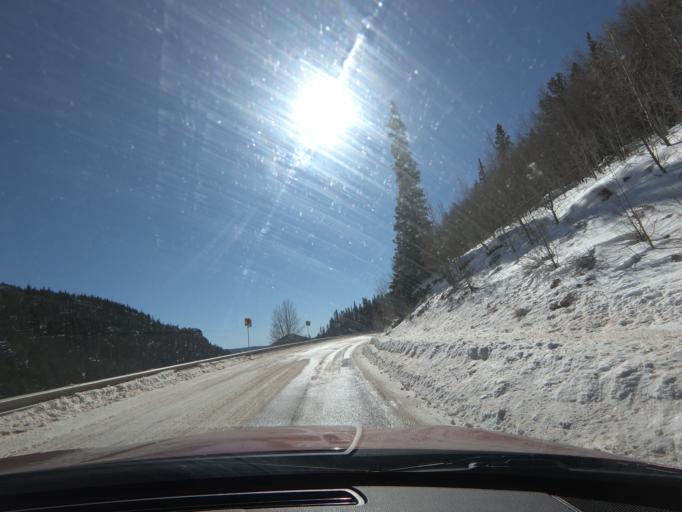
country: US
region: Colorado
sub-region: Teller County
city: Cripple Creek
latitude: 38.7511
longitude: -105.1023
